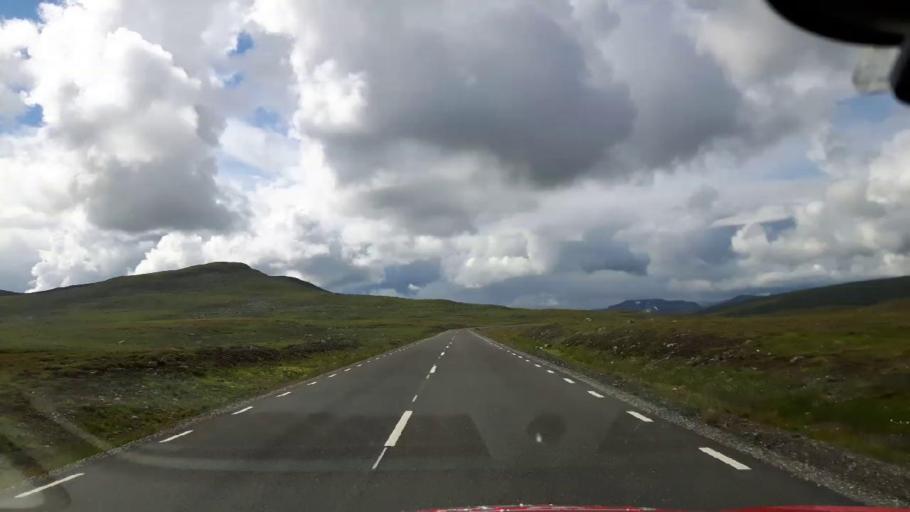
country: NO
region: Nordland
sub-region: Hattfjelldal
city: Hattfjelldal
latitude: 65.0610
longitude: 14.3755
